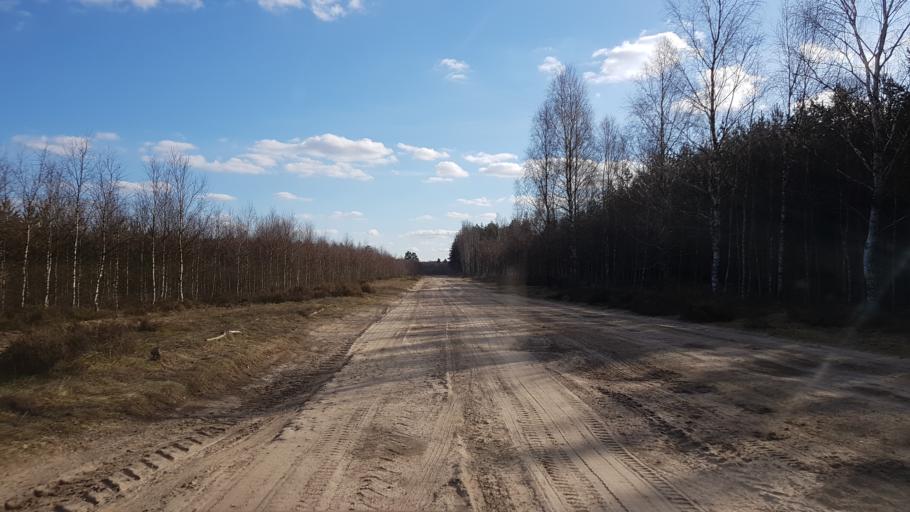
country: PL
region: Greater Poland Voivodeship
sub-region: Powiat zlotowski
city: Sypniewo
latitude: 53.5319
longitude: 16.6465
